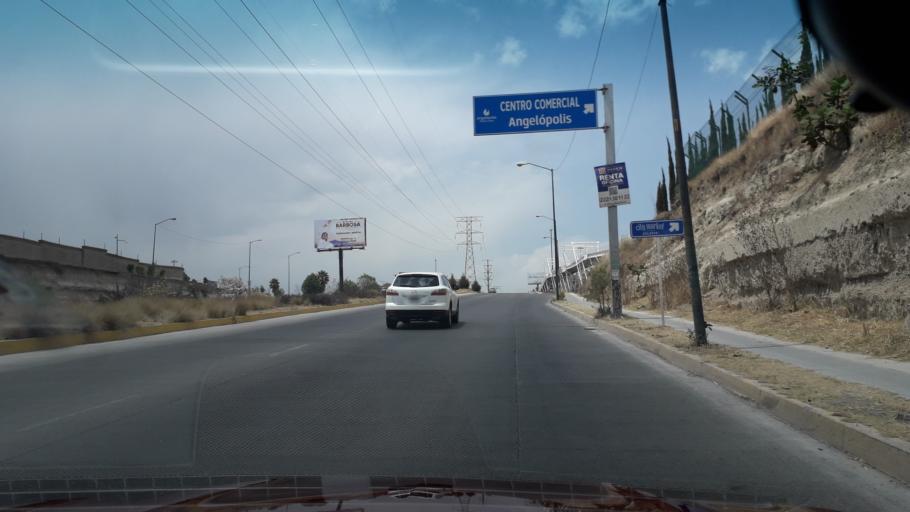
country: MX
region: Puebla
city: Tlazcalancingo
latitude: 19.0158
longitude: -98.2476
